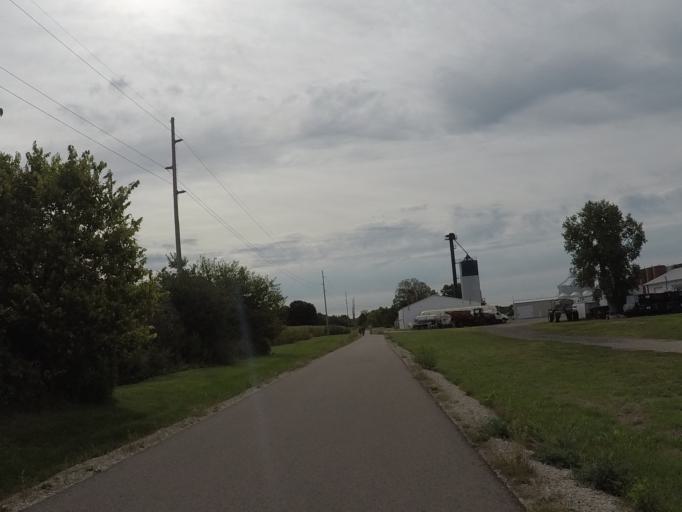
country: US
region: Wisconsin
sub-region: Sauk County
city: Prairie du Sac
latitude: 43.3172
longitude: -89.7382
